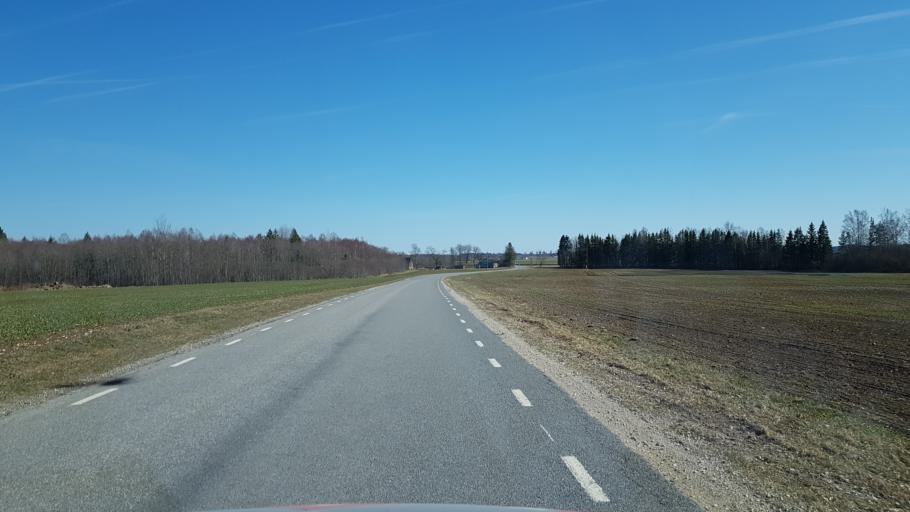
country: EE
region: Laeaene-Virumaa
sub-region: Someru vald
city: Someru
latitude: 59.3534
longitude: 26.4805
